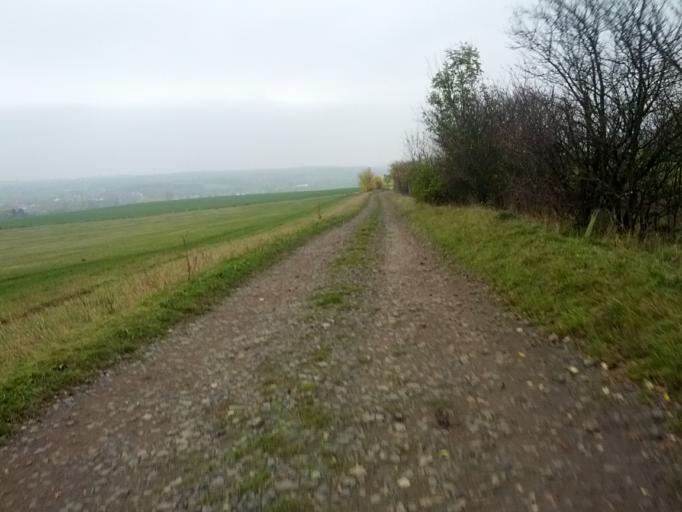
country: DE
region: Thuringia
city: Seebach
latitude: 50.9724
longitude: 10.4066
